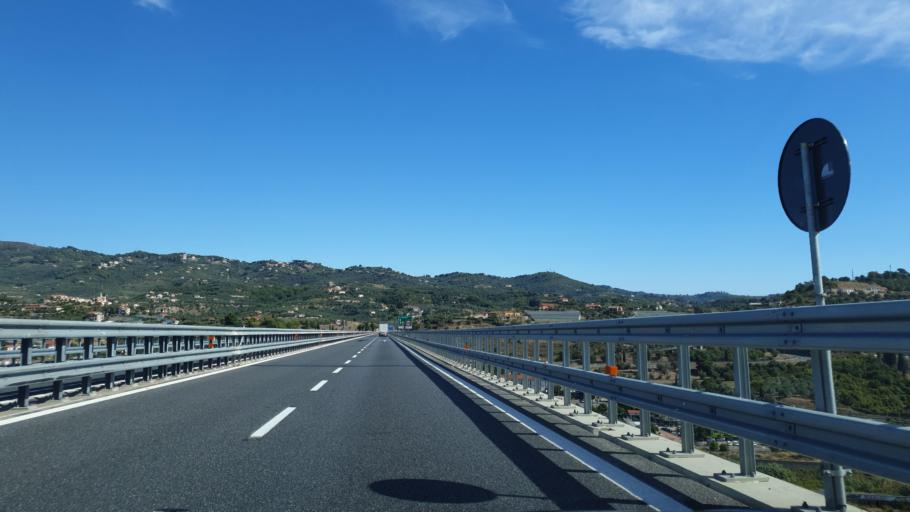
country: IT
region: Liguria
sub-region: Provincia di Imperia
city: San Lorenzo al Mare
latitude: 43.8717
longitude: 7.9917
